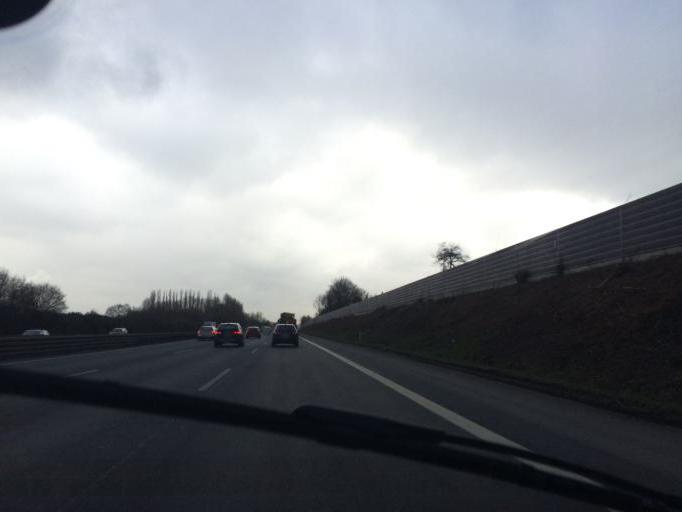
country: DE
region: North Rhine-Westphalia
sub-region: Regierungsbezirk Munster
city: Gladbeck
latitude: 51.5610
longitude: 7.0585
